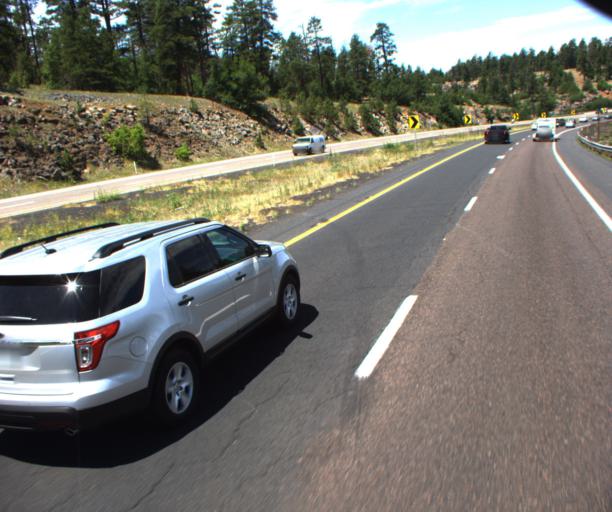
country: US
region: Arizona
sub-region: Coconino County
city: Sedona
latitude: 34.8641
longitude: -111.6232
